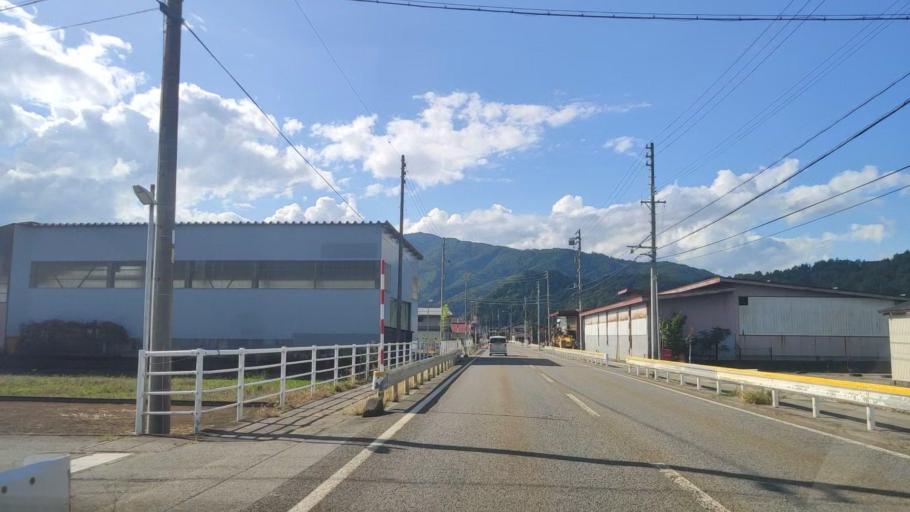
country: JP
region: Gifu
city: Takayama
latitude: 36.2583
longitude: 137.1515
